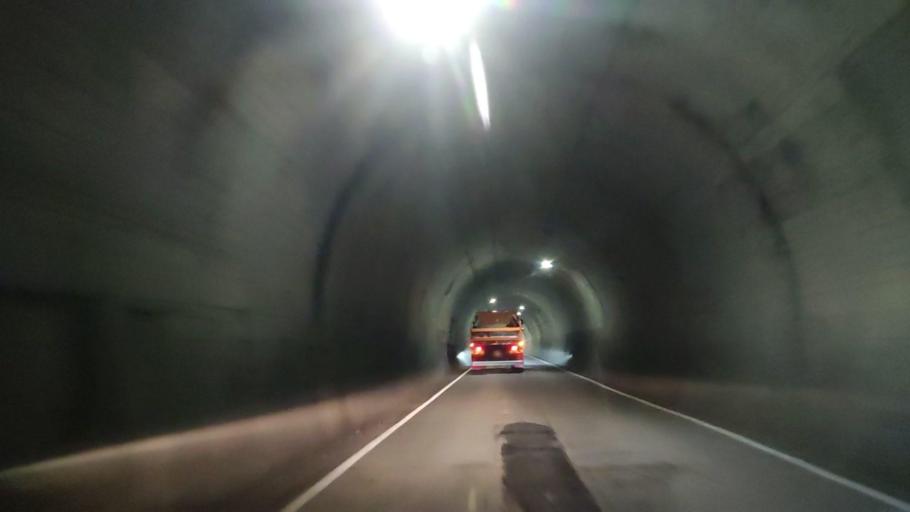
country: JP
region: Nagano
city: Iiyama
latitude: 36.8772
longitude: 138.3194
